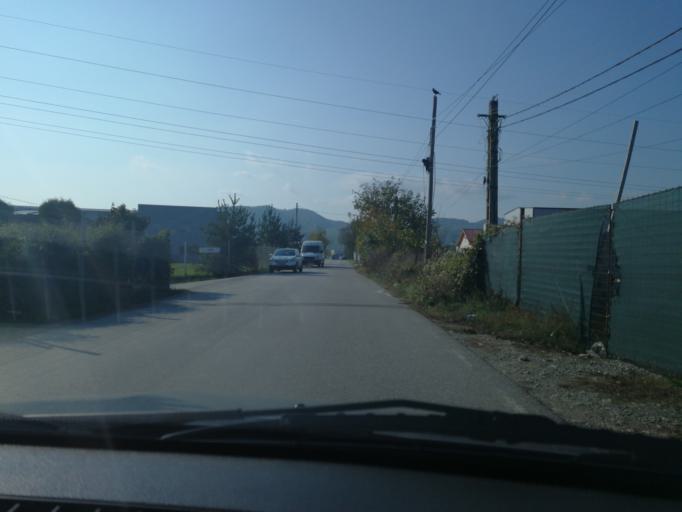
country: RO
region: Prahova
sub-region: Comuna Banesti
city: Banesti
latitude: 45.0951
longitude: 25.7602
